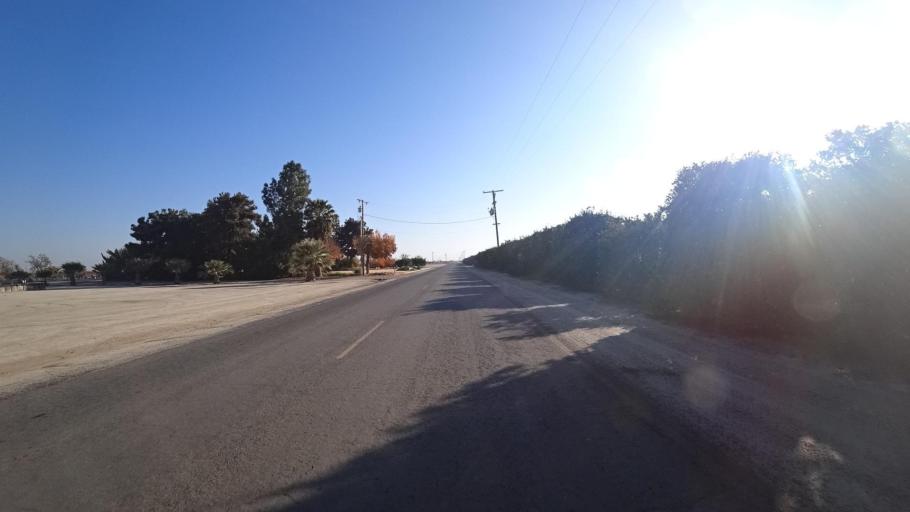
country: US
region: California
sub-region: Kern County
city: Delano
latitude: 35.7687
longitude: -119.1913
